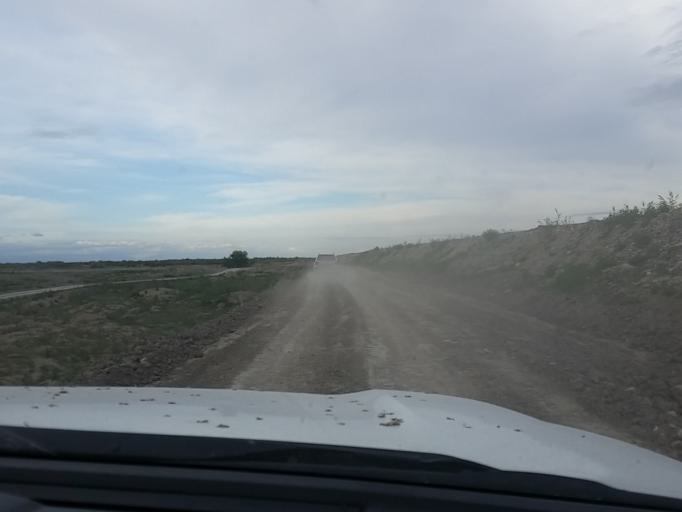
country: KZ
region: Almaty Oblysy
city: Zharkent
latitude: 44.1037
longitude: 80.0882
